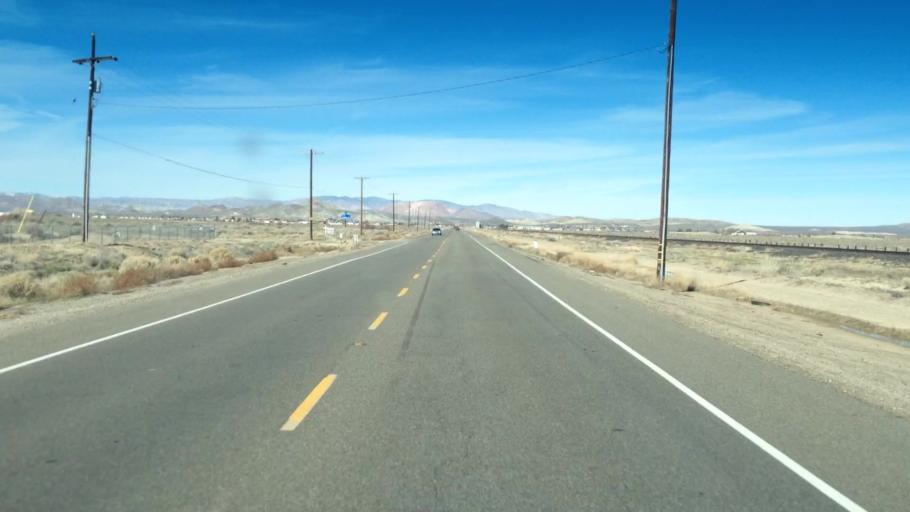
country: US
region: California
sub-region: Kern County
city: Rosamond
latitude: 34.8058
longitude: -118.1535
